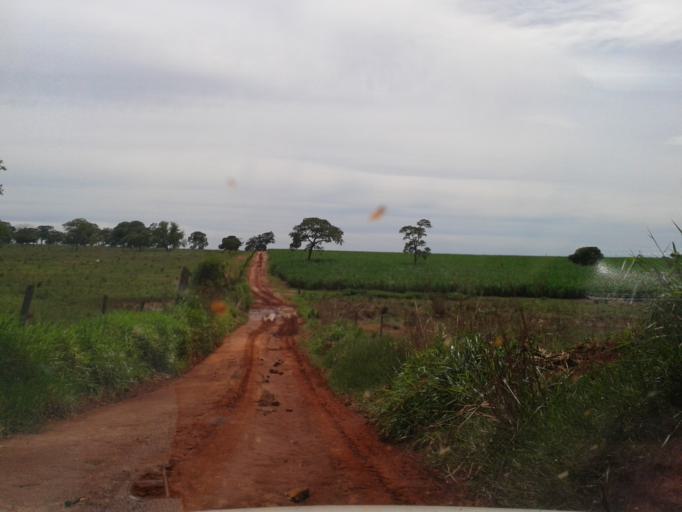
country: BR
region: Minas Gerais
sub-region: Santa Vitoria
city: Santa Vitoria
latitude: -19.2086
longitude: -50.6491
